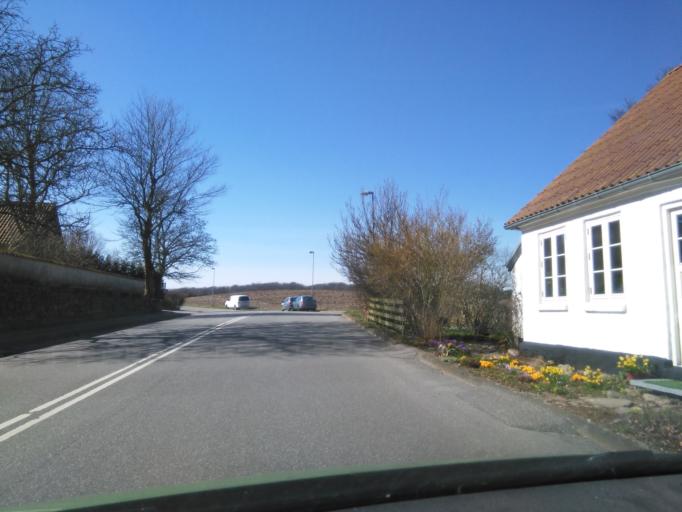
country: DK
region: Central Jutland
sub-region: Arhus Kommune
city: Lystrup
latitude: 56.2438
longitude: 10.2283
